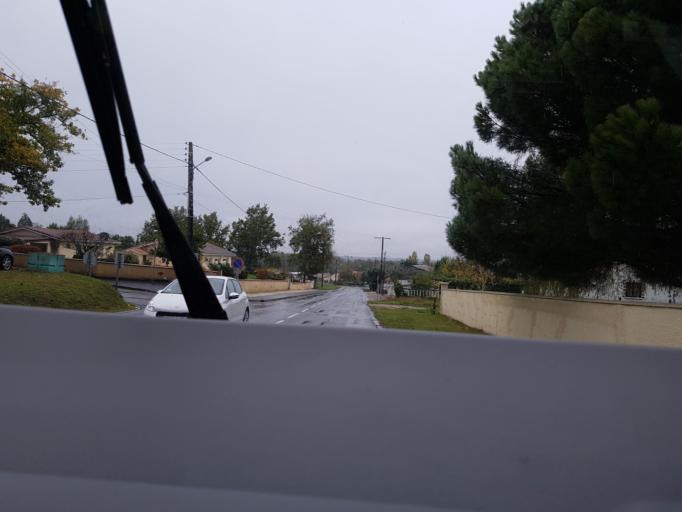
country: FR
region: Aquitaine
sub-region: Departement de la Gironde
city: Saint-Savin
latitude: 45.1398
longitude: -0.4418
